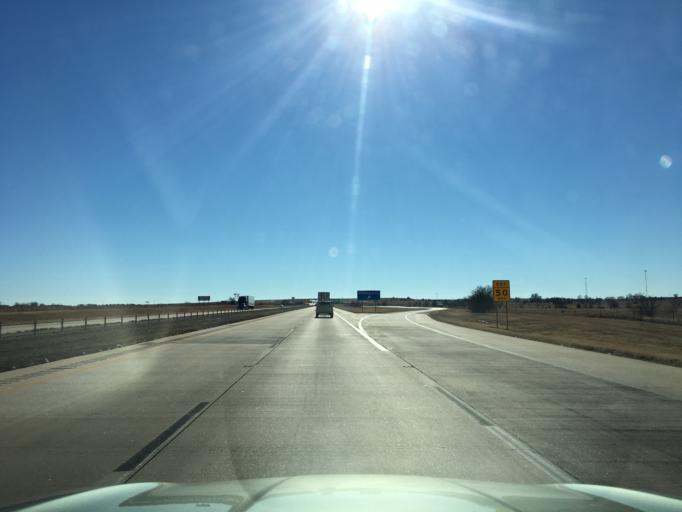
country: US
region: Oklahoma
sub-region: Noble County
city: Perry
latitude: 36.4161
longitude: -97.3272
